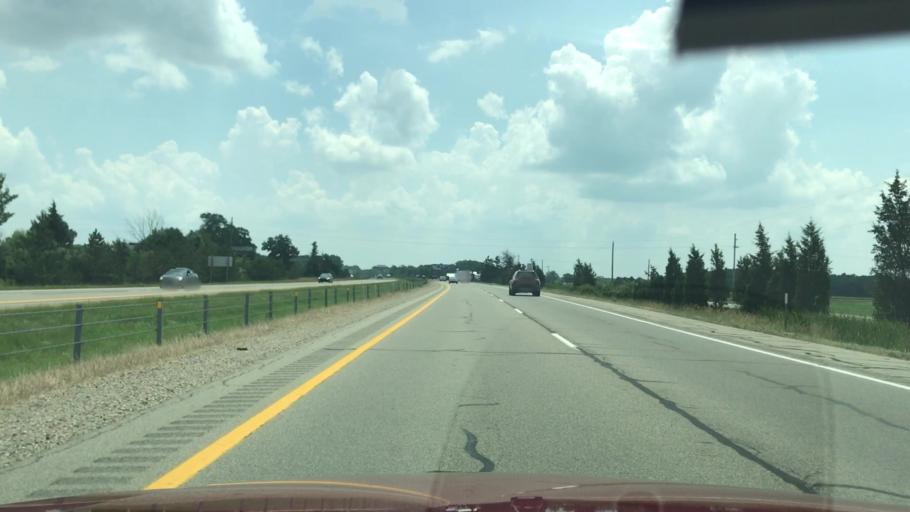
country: US
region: Michigan
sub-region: Allegan County
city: Wayland
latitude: 42.6225
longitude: -85.6625
